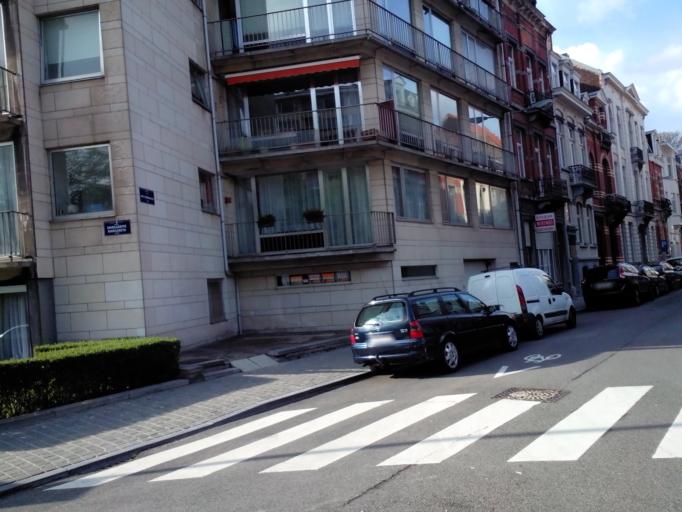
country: BE
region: Brussels Capital
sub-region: Bruxelles-Capitale
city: Brussels
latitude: 50.8472
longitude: 4.3857
